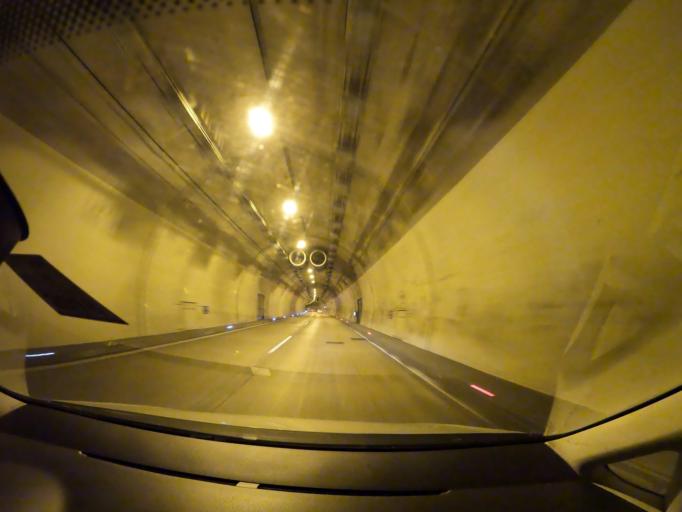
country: AT
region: Styria
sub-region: Politischer Bezirk Voitsberg
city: Modriach
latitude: 46.9610
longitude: 15.0624
